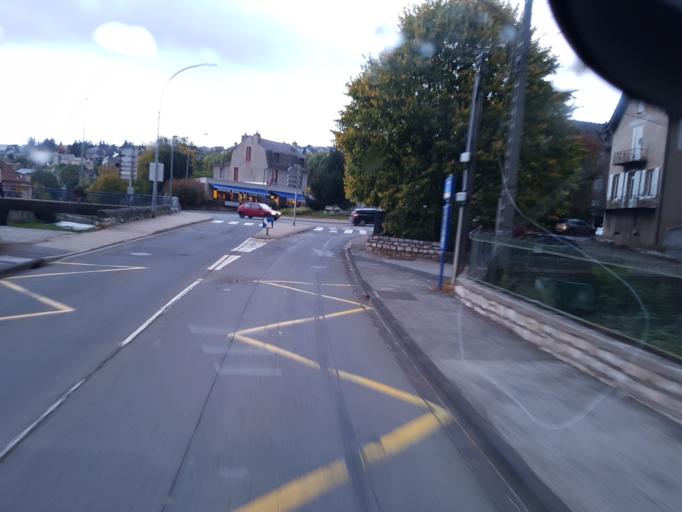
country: FR
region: Languedoc-Roussillon
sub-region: Departement de la Lozere
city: Mende
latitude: 44.5207
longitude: 3.5049
